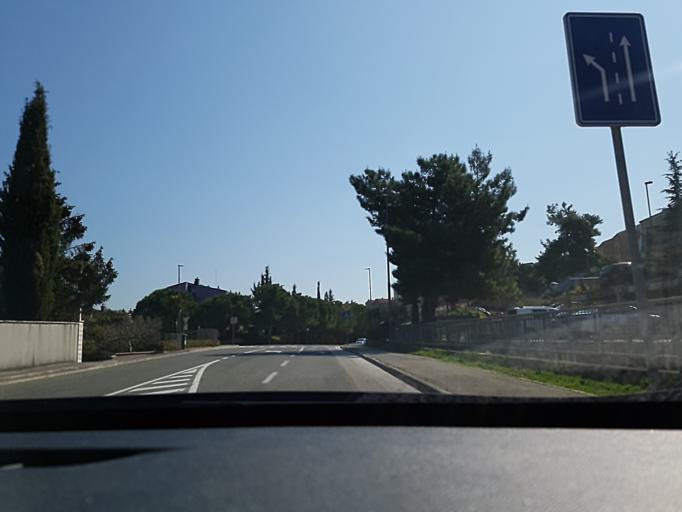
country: SI
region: Koper-Capodistria
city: Koper
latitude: 45.5421
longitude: 13.7063
